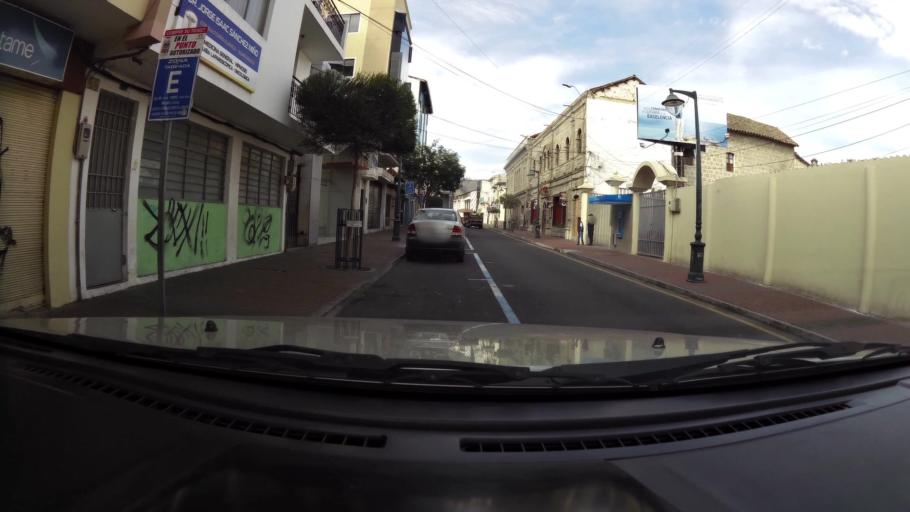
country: EC
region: Tungurahua
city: Ambato
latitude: -1.2399
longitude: -78.6287
